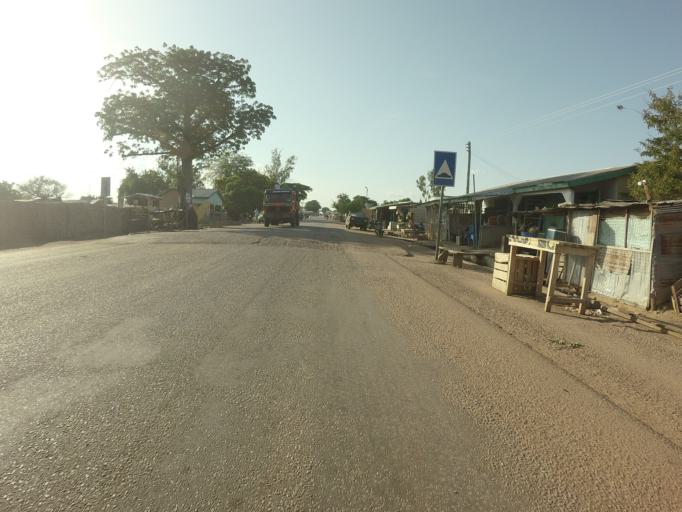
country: GH
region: Upper East
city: Navrongo
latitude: 10.9703
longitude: -1.1025
